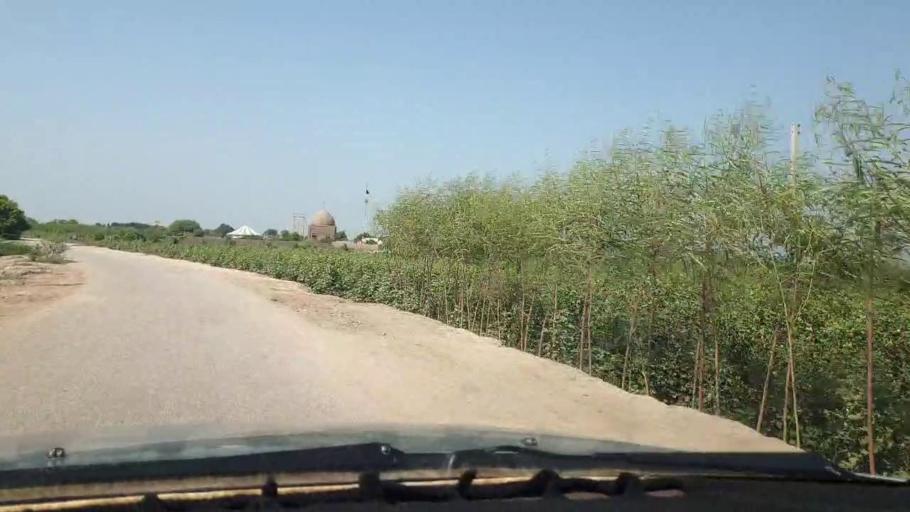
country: PK
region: Sindh
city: Chambar
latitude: 25.2290
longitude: 68.8693
